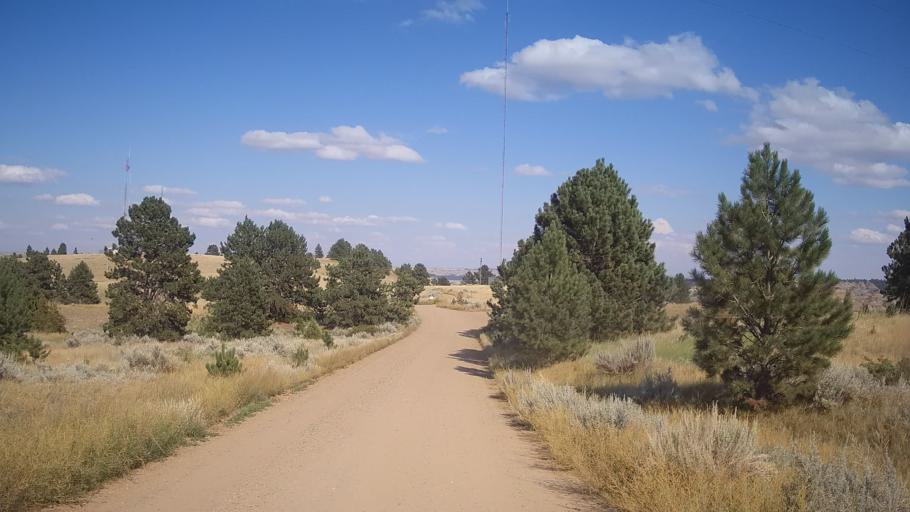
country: US
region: Montana
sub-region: Dawson County
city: Glendive
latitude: 47.0517
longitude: -104.6769
